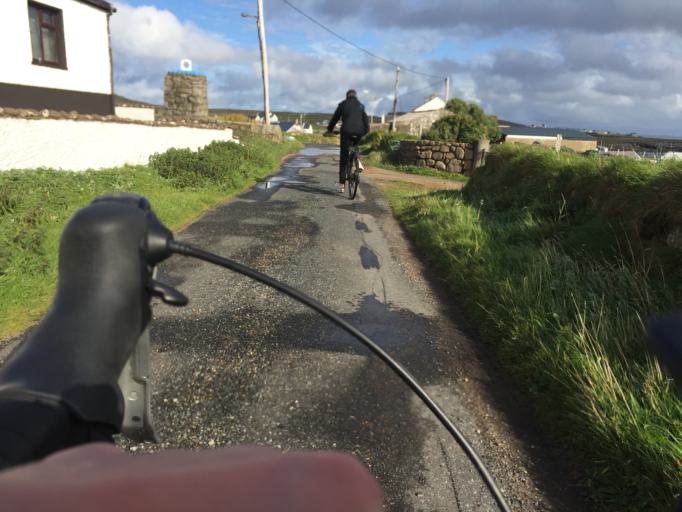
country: IE
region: Ulster
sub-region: County Donegal
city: Derrybeg
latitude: 55.2638
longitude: -8.2329
